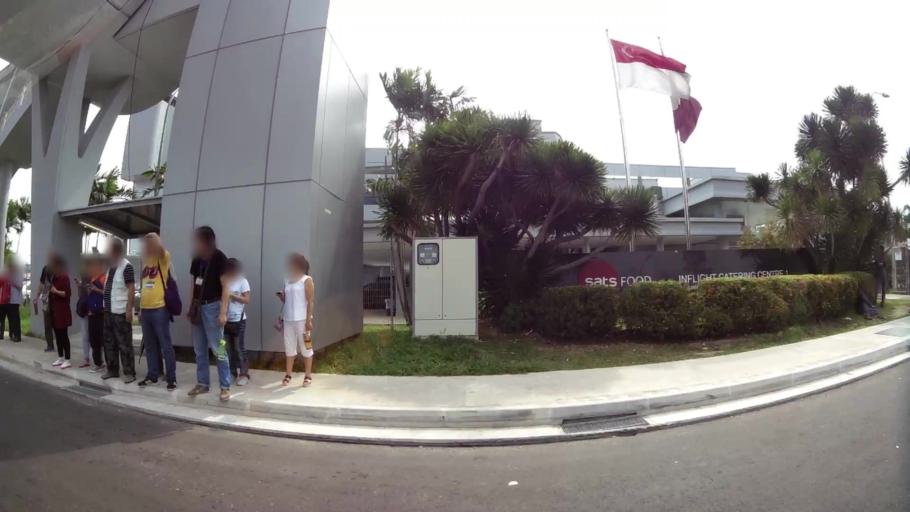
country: SG
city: Singapore
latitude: 1.3420
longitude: 103.9831
